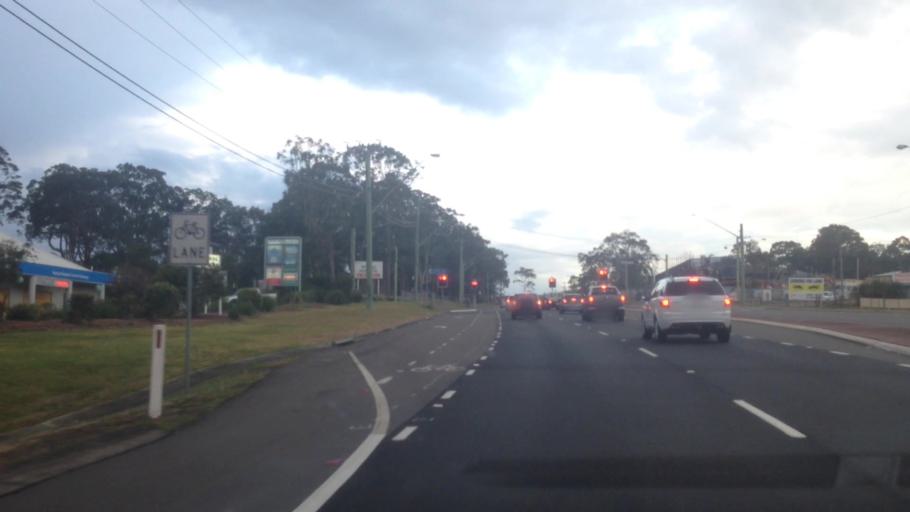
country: AU
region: New South Wales
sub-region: Wyong Shire
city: Kanwal
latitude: -33.2630
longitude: 151.4804
